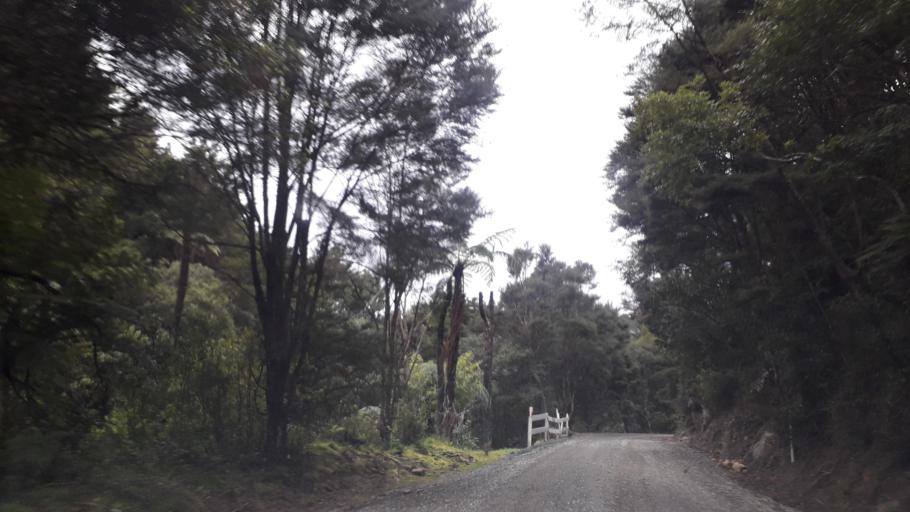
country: NZ
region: Northland
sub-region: Far North District
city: Waimate North
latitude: -35.1331
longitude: 173.7169
